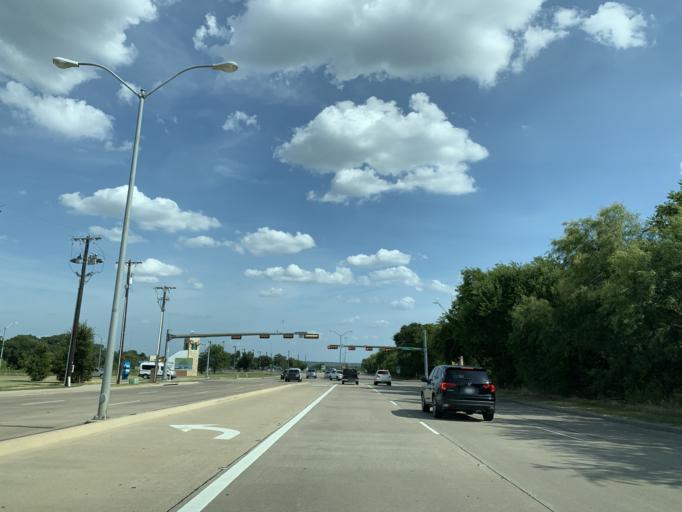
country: US
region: Texas
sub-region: Dallas County
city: Cedar Hill
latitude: 32.6356
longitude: -97.0451
